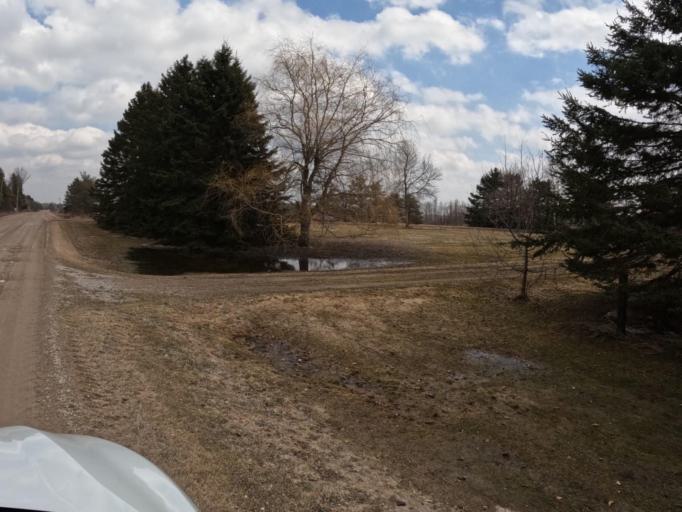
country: CA
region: Ontario
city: Shelburne
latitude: 44.0269
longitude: -80.2664
